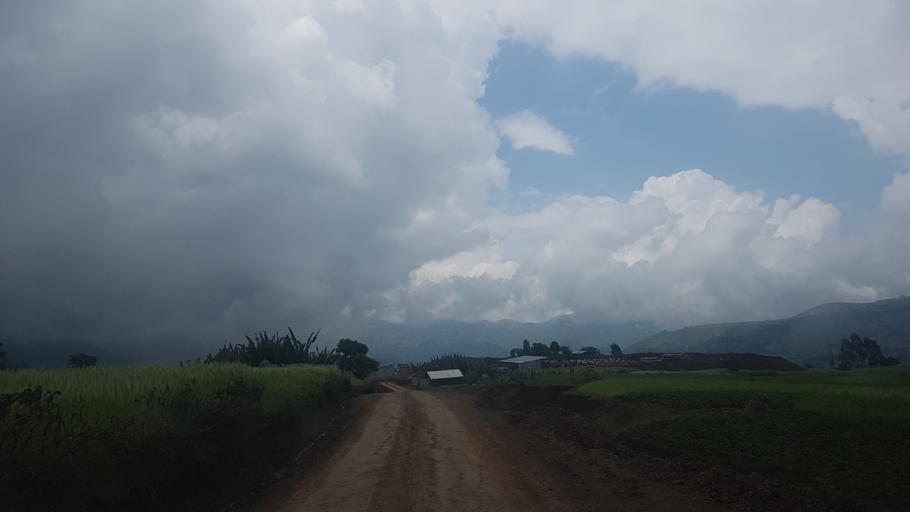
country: ET
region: Southern Nations, Nationalities, and People's Region
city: Arba Minch'
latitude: 6.3260
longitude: 37.5443
